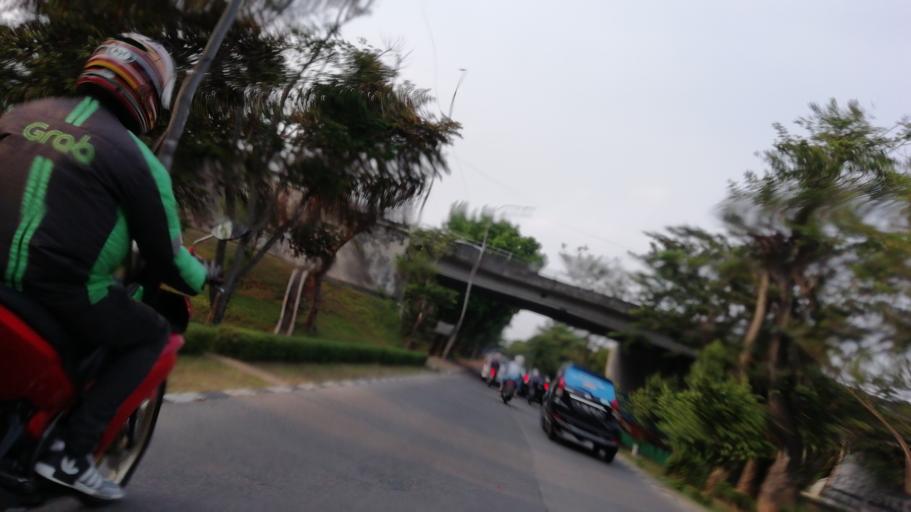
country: ID
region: West Java
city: Depok
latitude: -6.3562
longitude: 106.8314
